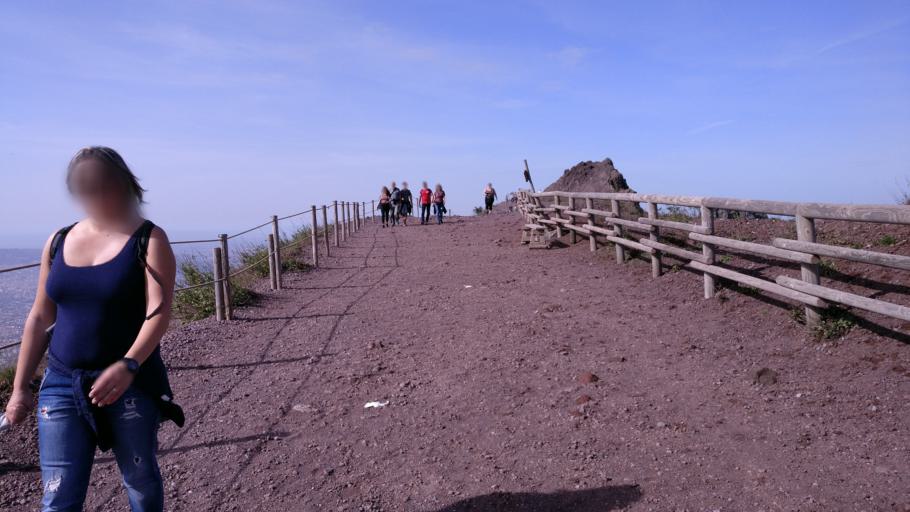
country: IT
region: Campania
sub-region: Provincia di Napoli
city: Torre del Greco
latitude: 40.8194
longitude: 14.4242
